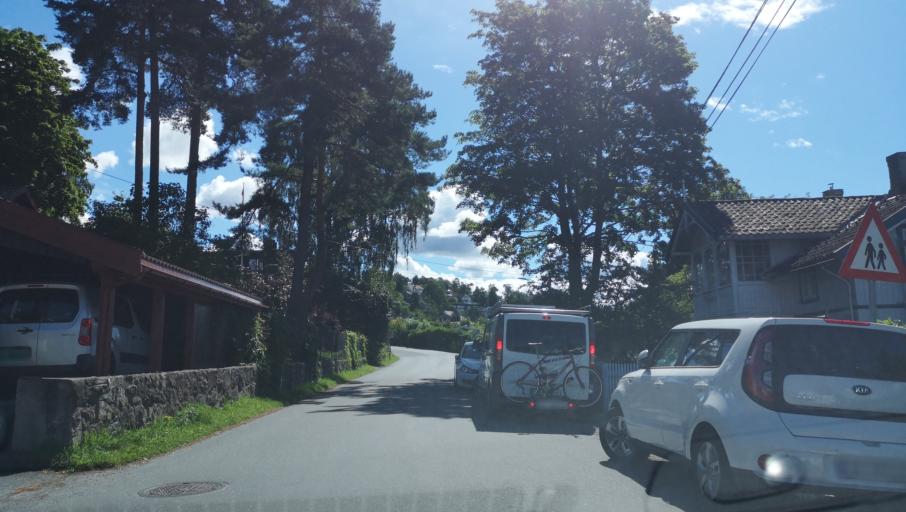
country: NO
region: Akershus
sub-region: Frogn
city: Drobak
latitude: 59.6549
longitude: 10.6353
